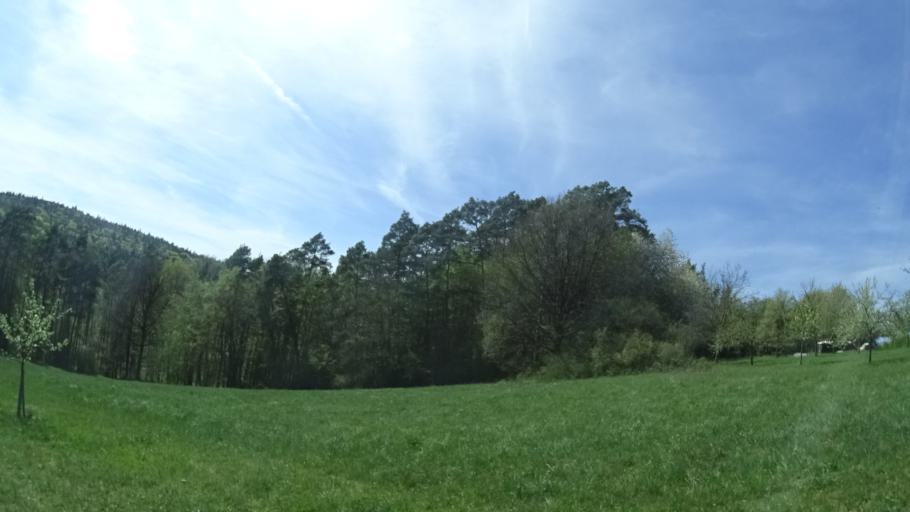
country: DE
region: Bavaria
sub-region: Regierungsbezirk Unterfranken
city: Burgpreppach
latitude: 50.1731
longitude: 10.6310
